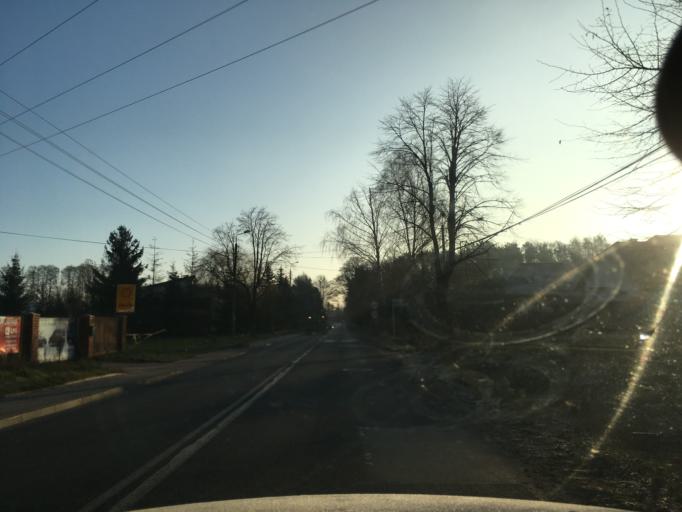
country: PL
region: Masovian Voivodeship
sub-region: Powiat piaseczynski
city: Piaseczno
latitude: 52.0713
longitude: 20.9787
